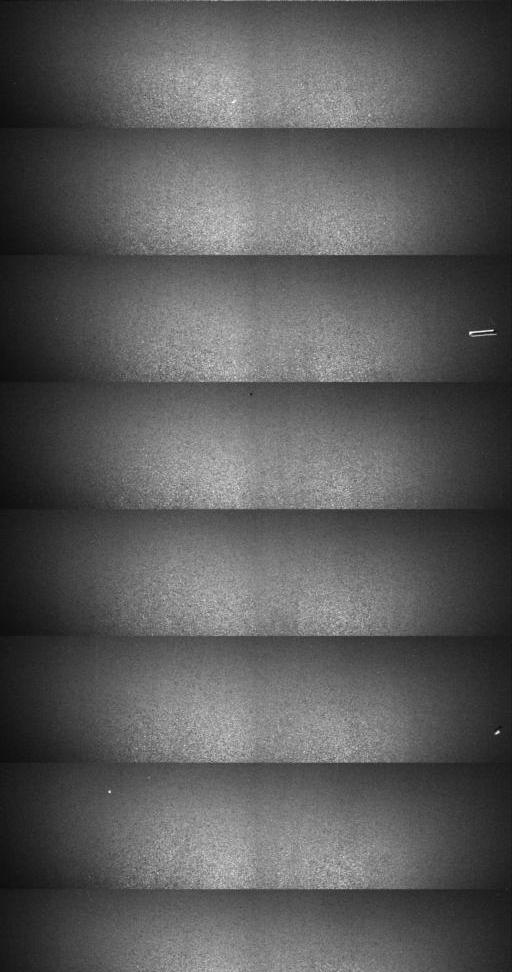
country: US
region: Vermont
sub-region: Franklin County
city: Richford
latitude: 44.9772
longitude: -72.5197
